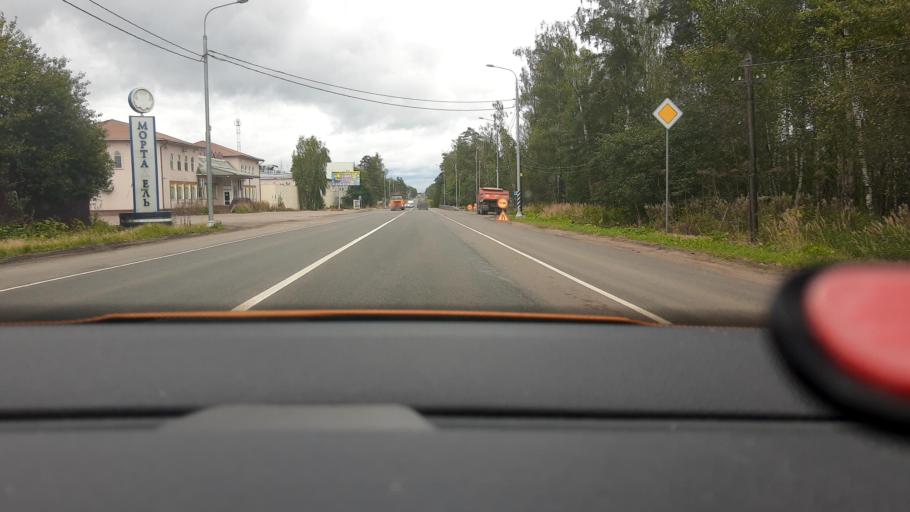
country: RU
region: Moskovskaya
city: Lesnoy
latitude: 56.0678
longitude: 38.0249
